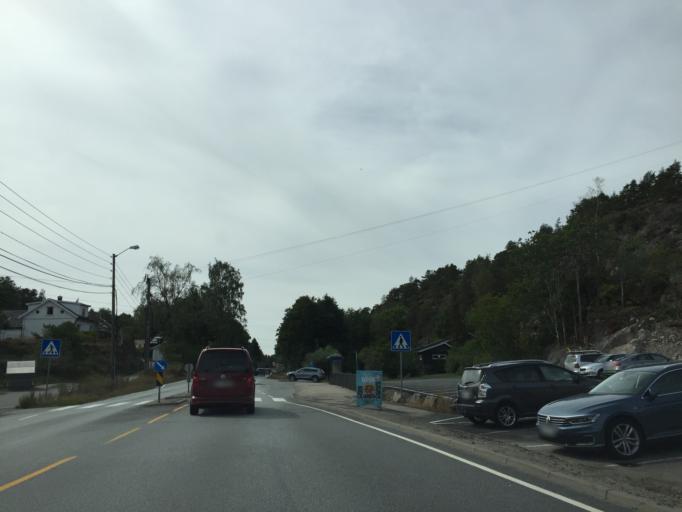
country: NO
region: Ostfold
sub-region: Fredrikstad
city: Fredrikstad
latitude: 59.1103
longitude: 10.9101
